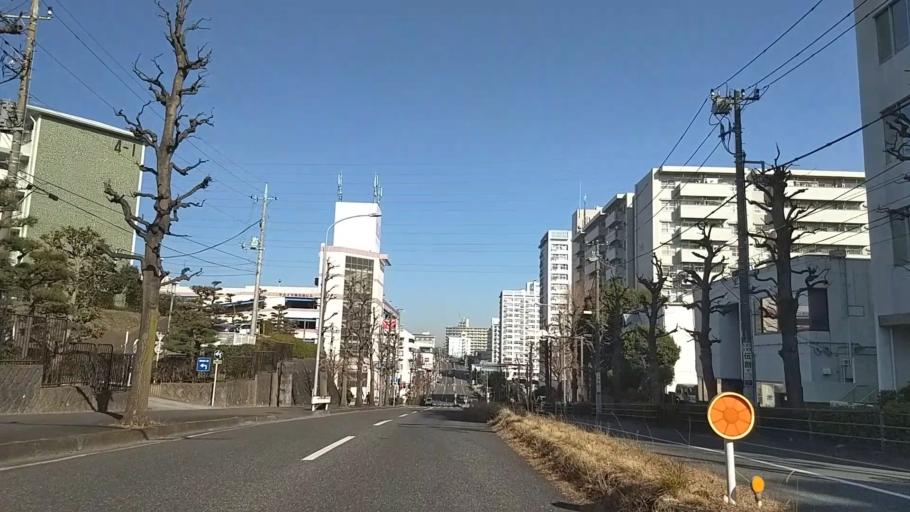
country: JP
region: Kanagawa
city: Kamakura
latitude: 35.3761
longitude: 139.5967
